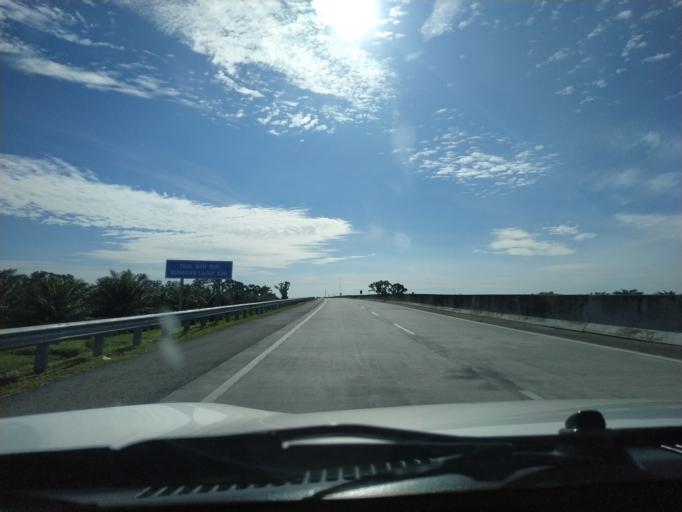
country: ID
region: North Sumatra
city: Perbaungan
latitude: 3.5327
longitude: 98.8723
